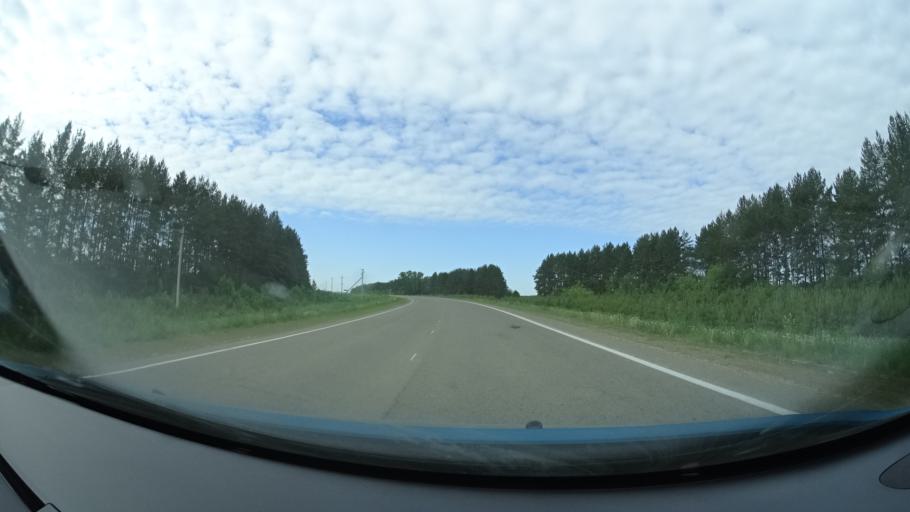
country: RU
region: Perm
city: Kuyeda
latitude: 56.4812
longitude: 55.5924
